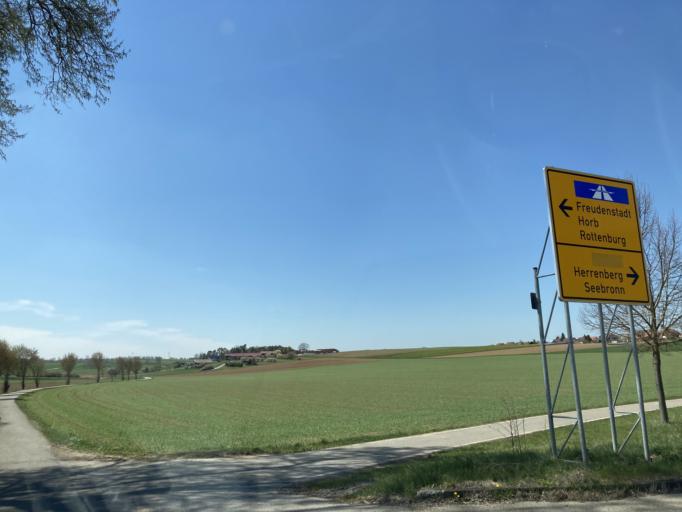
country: DE
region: Baden-Wuerttemberg
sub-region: Tuebingen Region
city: Rottenburg
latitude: 48.5037
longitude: 8.8898
